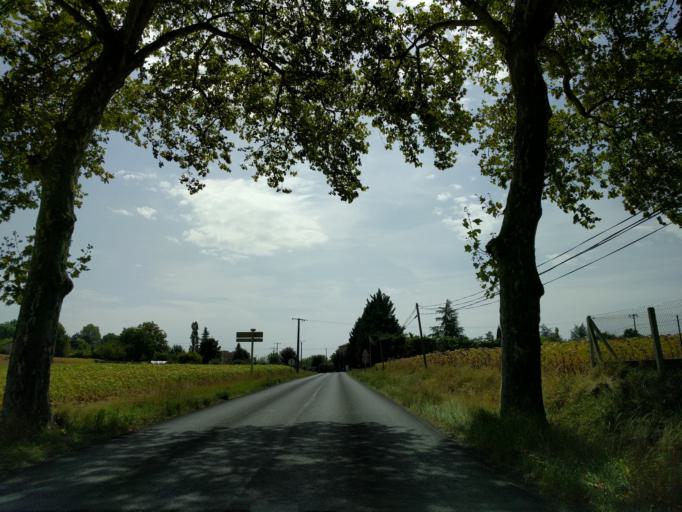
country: FR
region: Midi-Pyrenees
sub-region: Departement du Tarn
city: Saix
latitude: 43.6334
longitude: 2.2006
